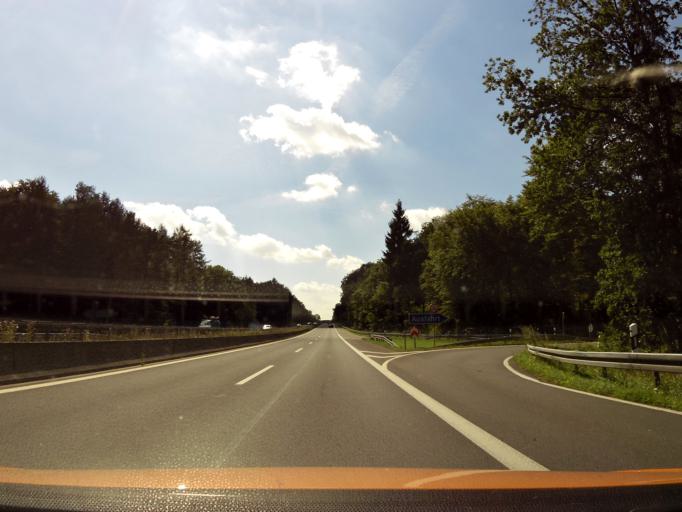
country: DE
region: Brandenburg
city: Gramzow
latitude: 53.1846
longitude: 13.9307
